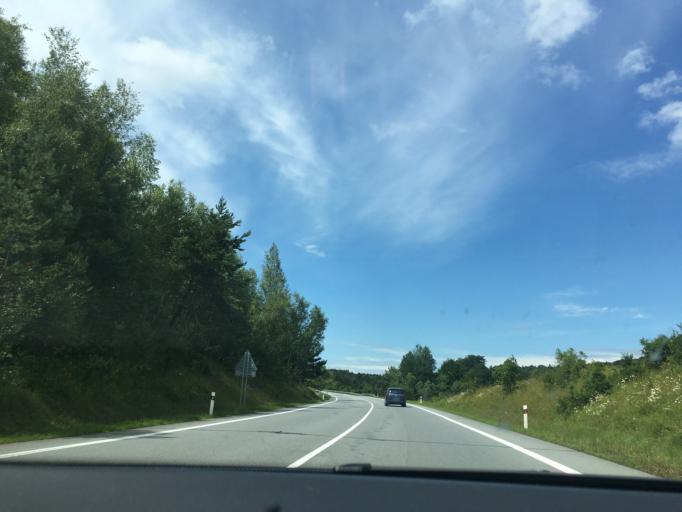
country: PL
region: Subcarpathian Voivodeship
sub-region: Powiat krosnienski
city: Jasliska
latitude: 49.4041
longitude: 21.7036
